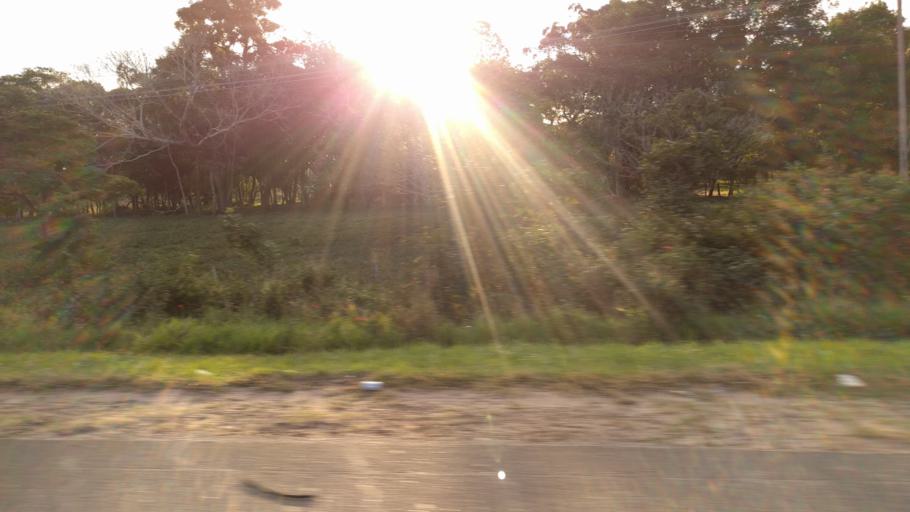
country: BO
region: Santa Cruz
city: Buena Vista
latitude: -17.4312
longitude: -63.6330
